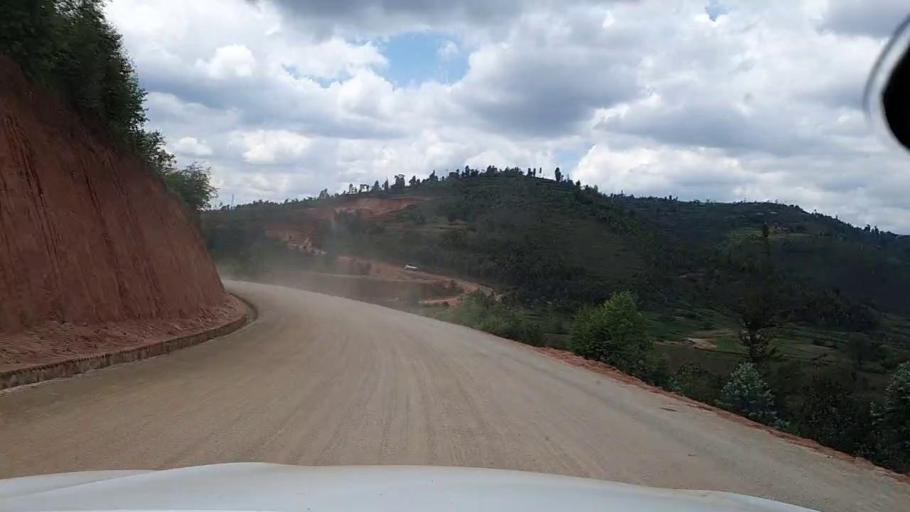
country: RW
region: Southern Province
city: Butare
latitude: -2.6946
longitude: 29.5548
